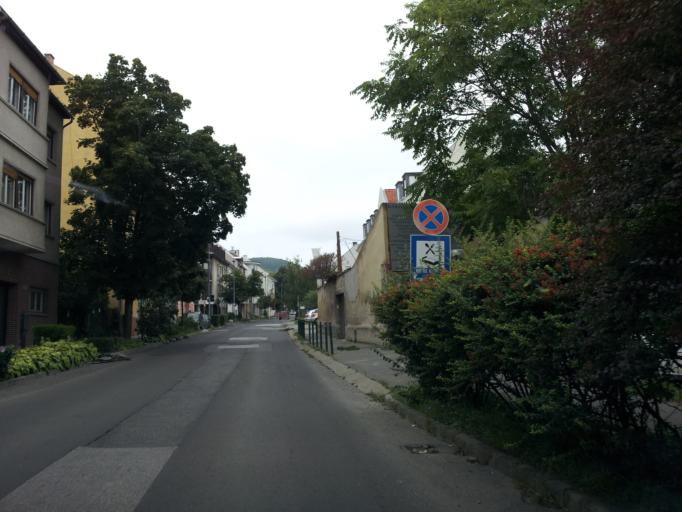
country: HU
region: Budapest
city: Budapest II. keruelet
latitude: 47.5261
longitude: 19.0356
